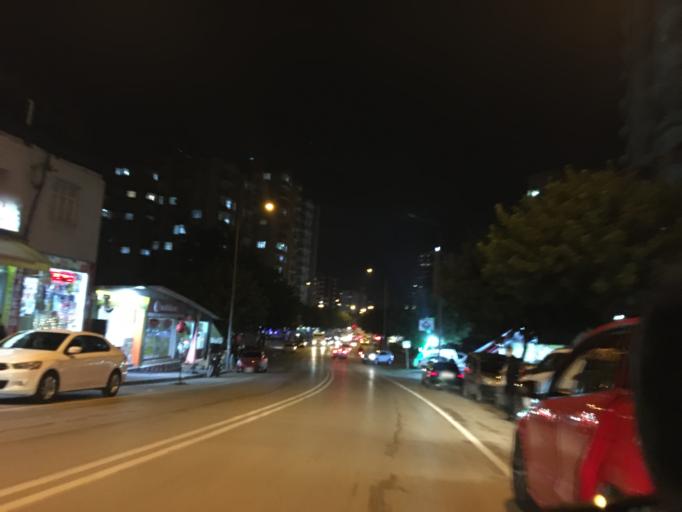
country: TR
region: Adana
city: Seyhan
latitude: 37.0243
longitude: 35.2831
